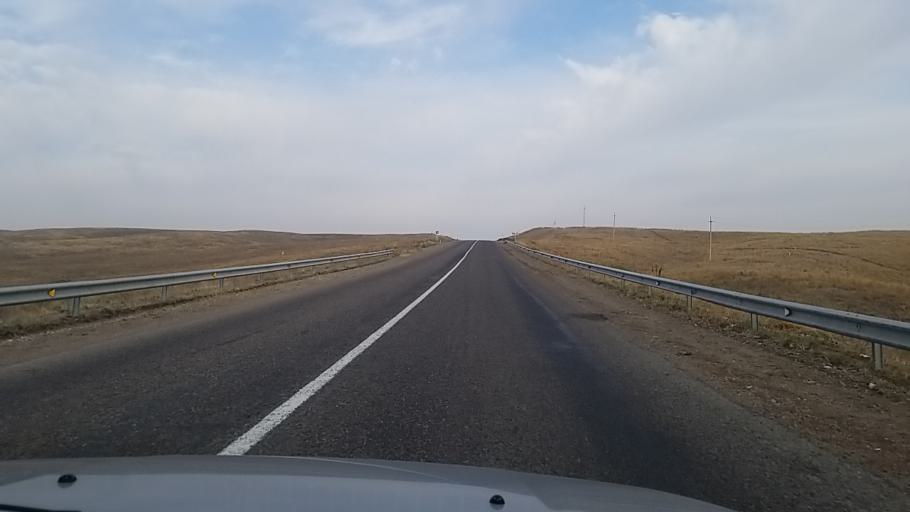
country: KZ
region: Almaty Oblysy
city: Burunday
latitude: 43.4922
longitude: 76.6653
